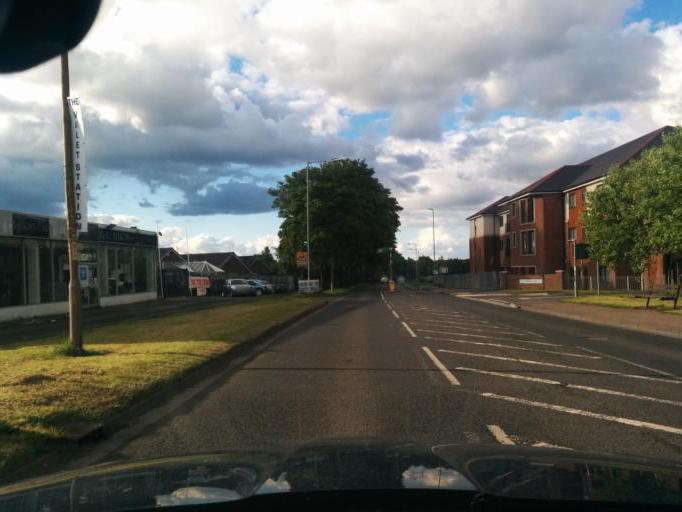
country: GB
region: England
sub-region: Northumberland
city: Bedlington
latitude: 55.1345
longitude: -1.5997
